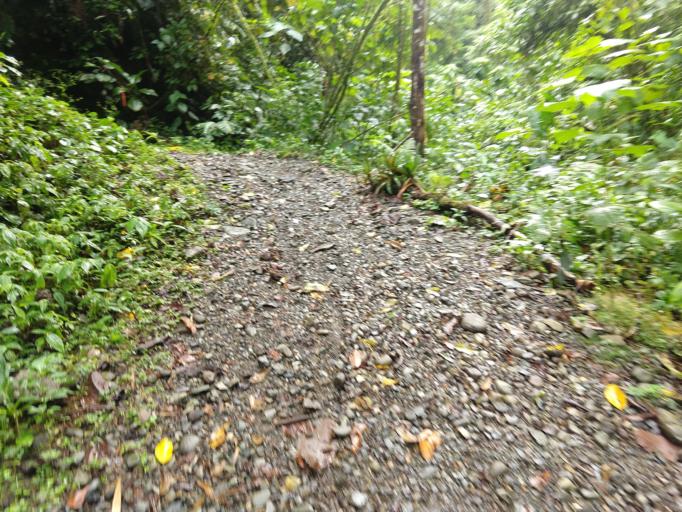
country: CR
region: Cartago
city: Orosi
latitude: 9.7437
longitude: -83.8335
